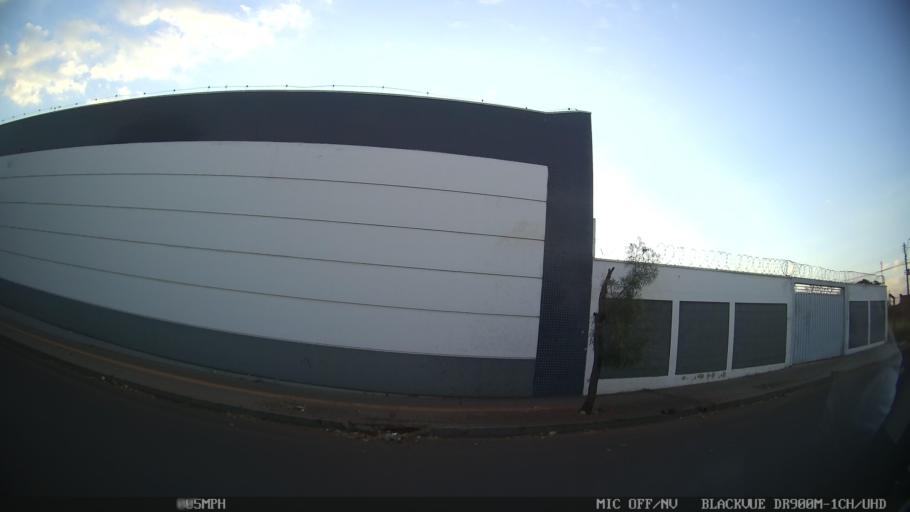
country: BR
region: Sao Paulo
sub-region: Ribeirao Preto
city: Ribeirao Preto
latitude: -21.1468
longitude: -47.7889
